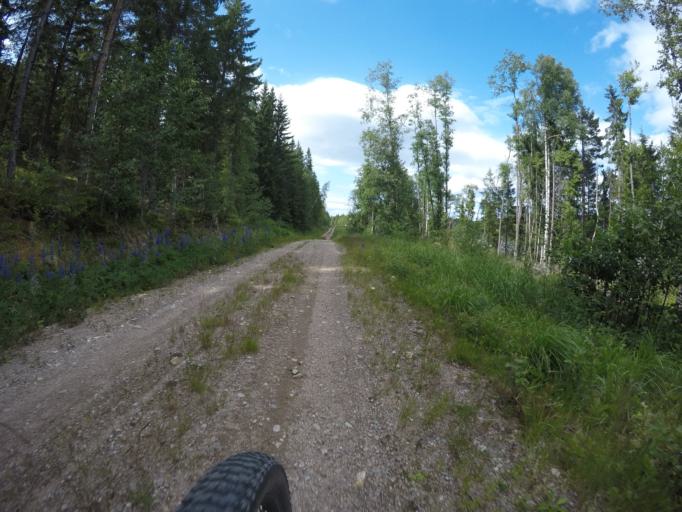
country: SE
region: Dalarna
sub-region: Ludvika Kommun
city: Abborrberget
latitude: 60.0328
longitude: 14.5992
